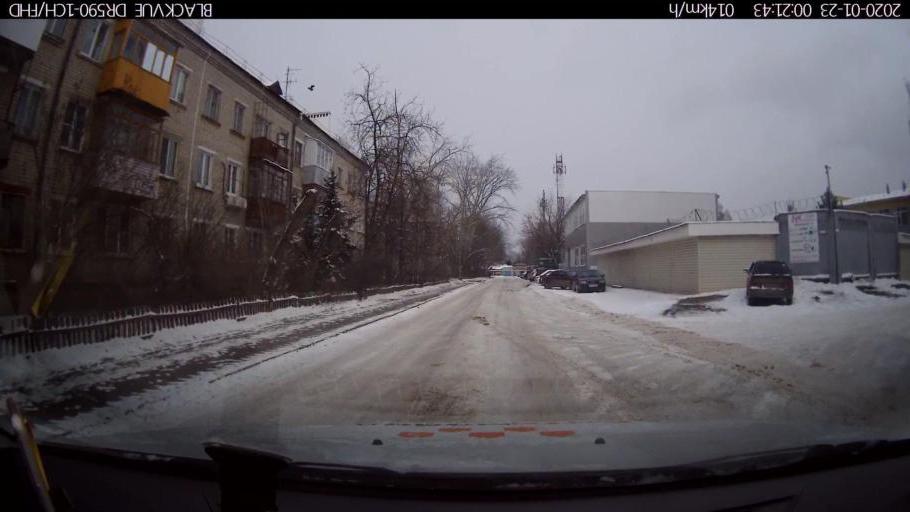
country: RU
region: Nizjnij Novgorod
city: Gorbatovka
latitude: 56.3634
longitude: 43.8290
